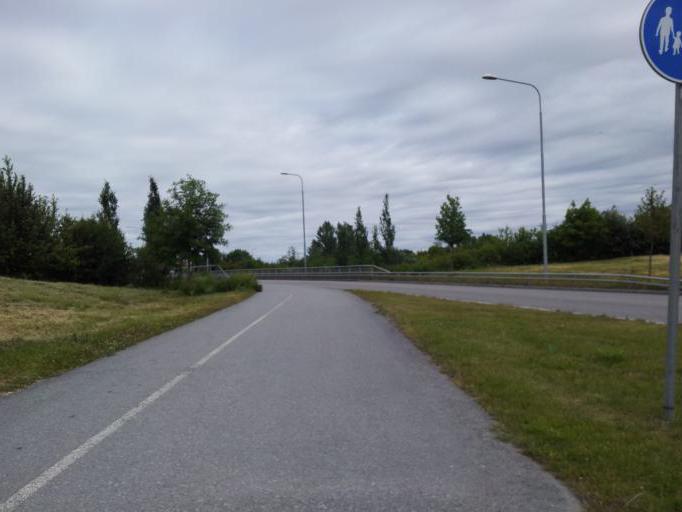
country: SE
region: Uppsala
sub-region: Uppsala Kommun
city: Gamla Uppsala
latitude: 59.8822
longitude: 17.6457
